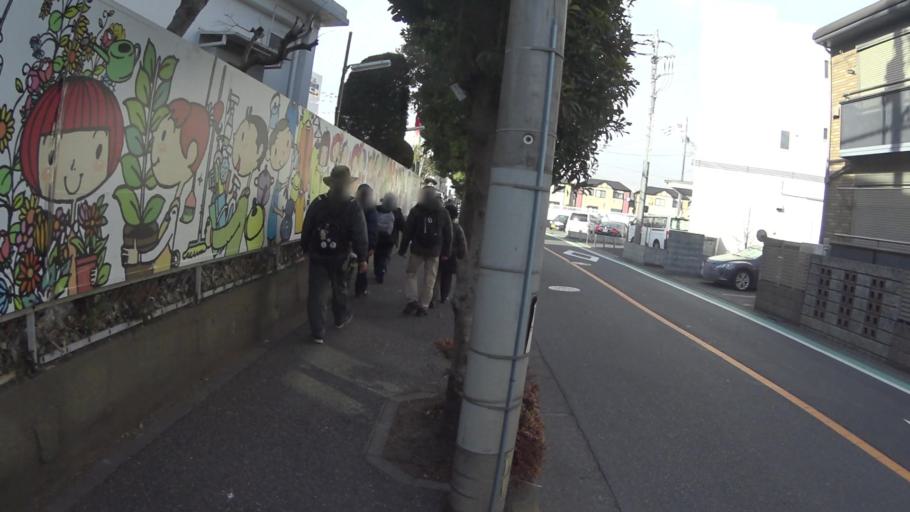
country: JP
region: Tokyo
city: Kokubunji
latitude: 35.6584
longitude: 139.4803
